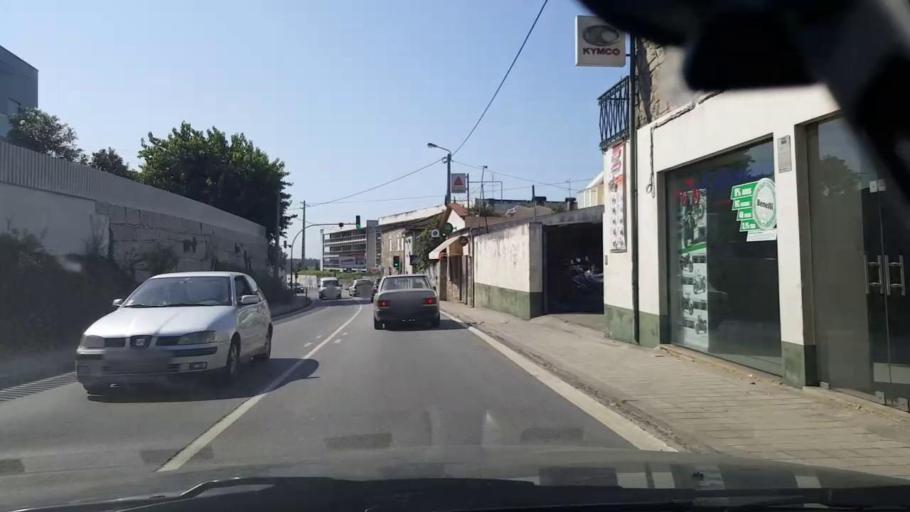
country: PT
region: Porto
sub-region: Povoa de Varzim
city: Pedroso
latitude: 41.4018
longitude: -8.6824
